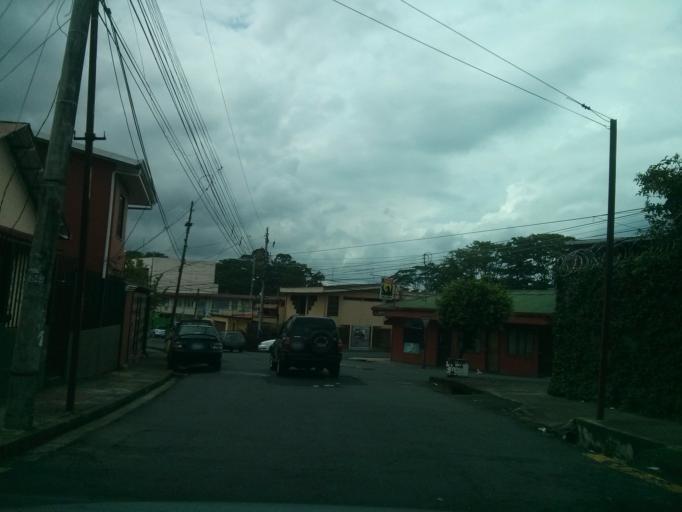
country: CR
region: San Jose
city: San Pedro
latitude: 9.9253
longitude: -84.0540
